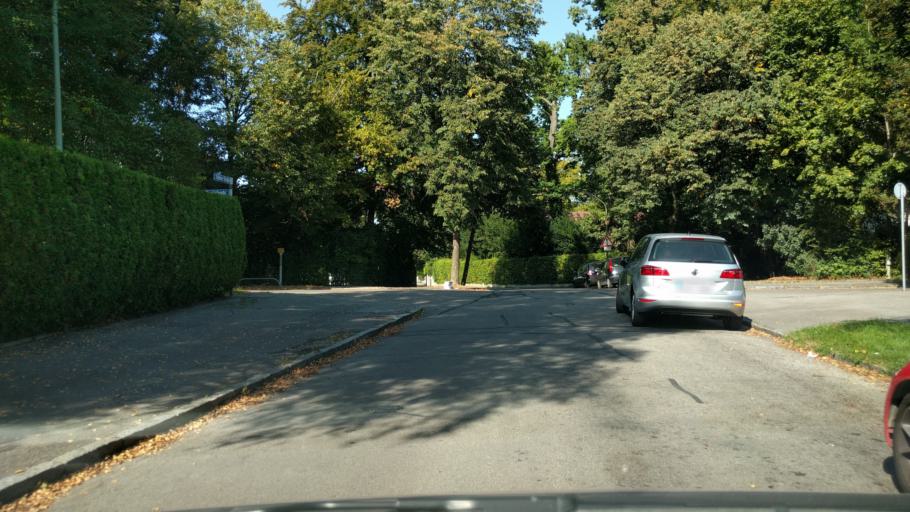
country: DE
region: Bavaria
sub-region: Upper Bavaria
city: Pullach im Isartal
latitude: 48.0723
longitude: 11.5265
